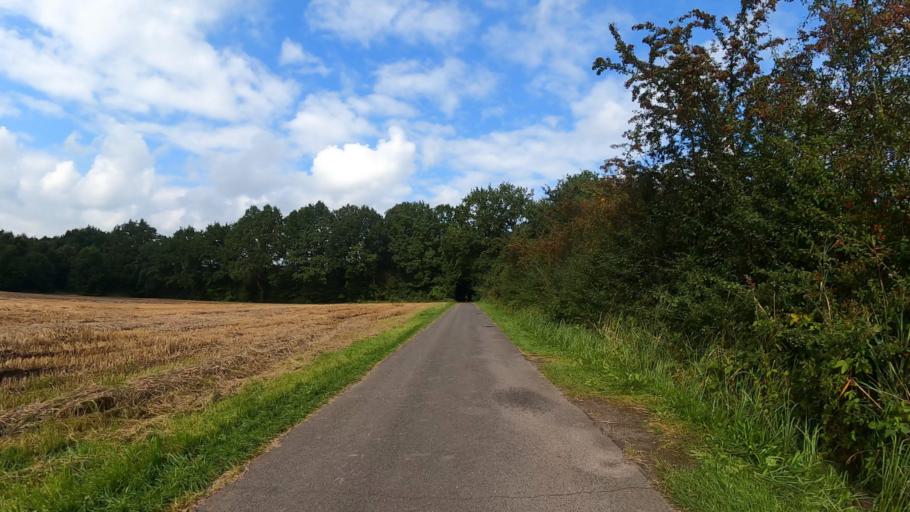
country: DE
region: Schleswig-Holstein
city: Kolln-Reisiek
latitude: 53.7263
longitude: 9.6843
